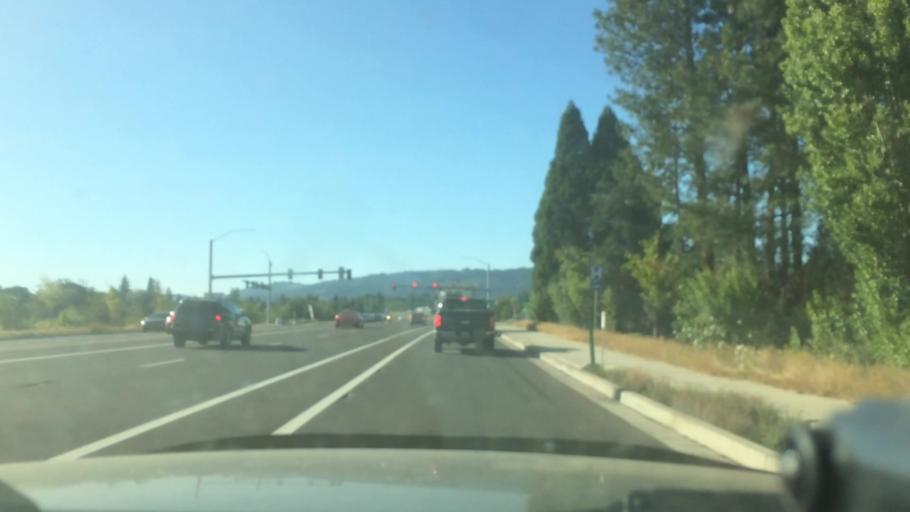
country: US
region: Oregon
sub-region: Yamhill County
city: Newberg
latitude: 45.2926
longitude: -122.9488
